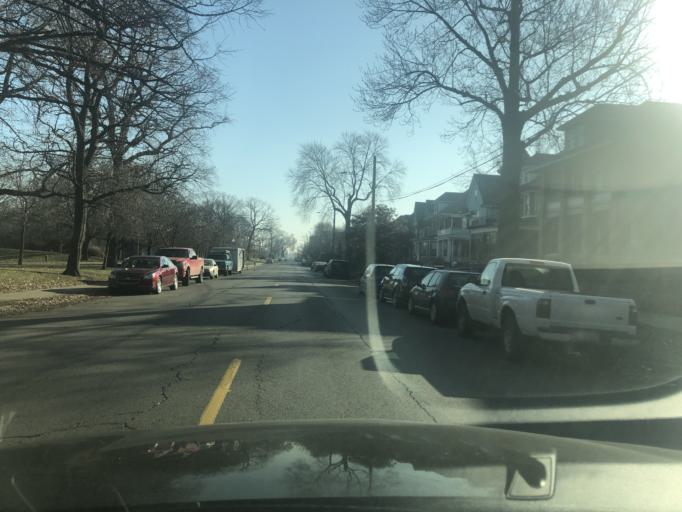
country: US
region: Michigan
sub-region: Wayne County
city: Detroit
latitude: 42.3189
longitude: -83.0949
